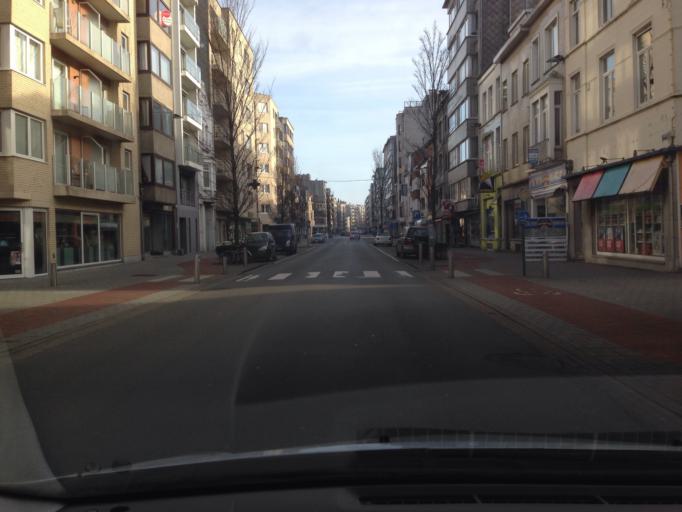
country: BE
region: Flanders
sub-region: Provincie West-Vlaanderen
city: Ostend
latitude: 51.2225
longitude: 2.9086
